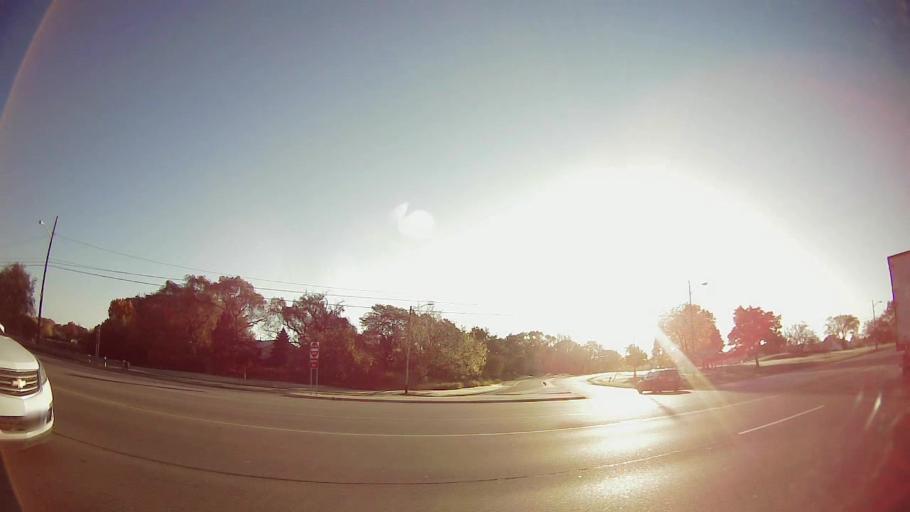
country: US
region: Michigan
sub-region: Macomb County
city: Center Line
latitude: 42.5252
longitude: -83.0292
